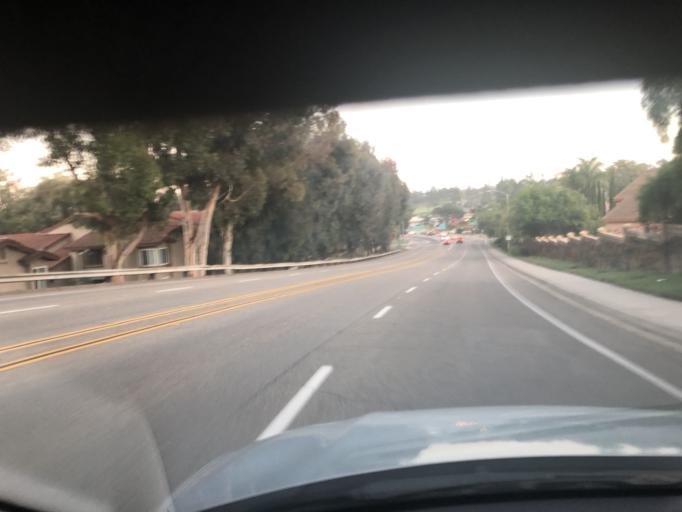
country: US
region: California
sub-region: San Diego County
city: Chula Vista
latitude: 32.6489
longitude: -117.0687
